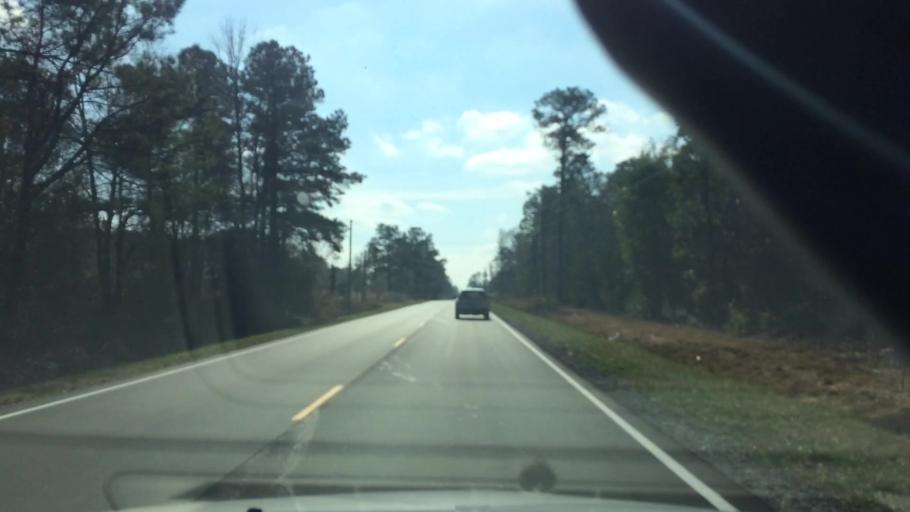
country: US
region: North Carolina
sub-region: Duplin County
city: Beulaville
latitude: 34.9853
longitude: -77.7587
